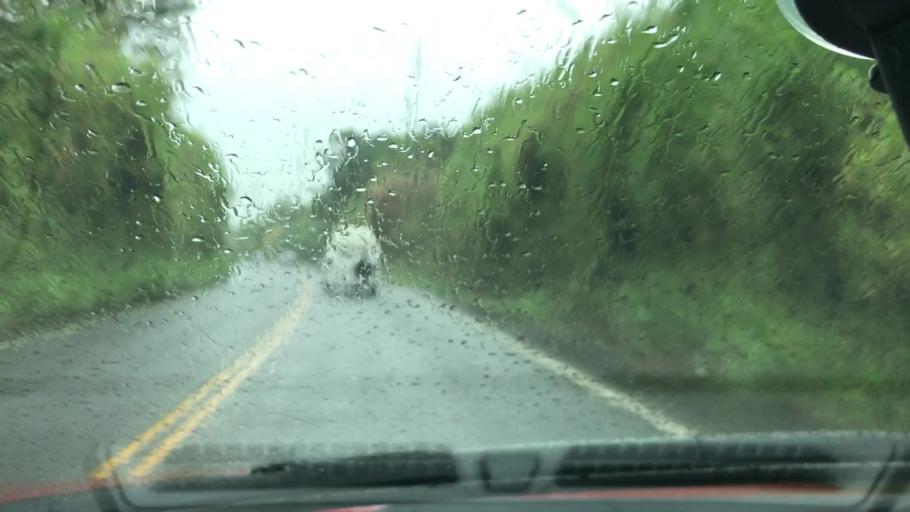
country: US
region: Hawaii
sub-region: Hawaii County
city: Pepeekeo
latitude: 19.9861
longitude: -155.2410
